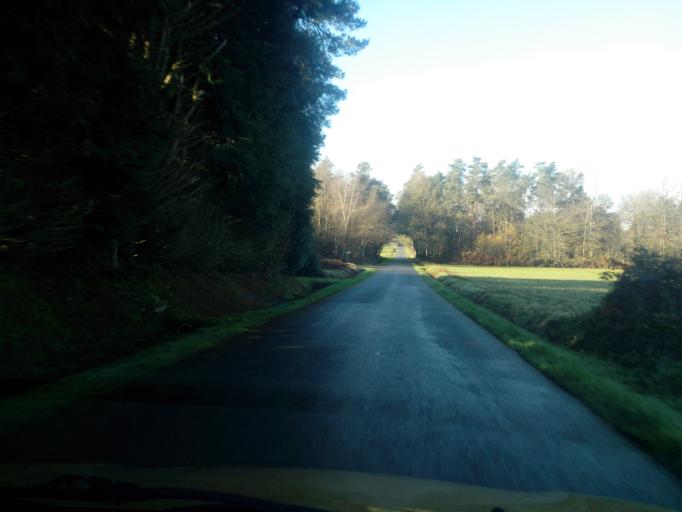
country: FR
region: Brittany
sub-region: Departement du Morbihan
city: Pleucadeuc
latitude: 47.7270
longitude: -2.3906
